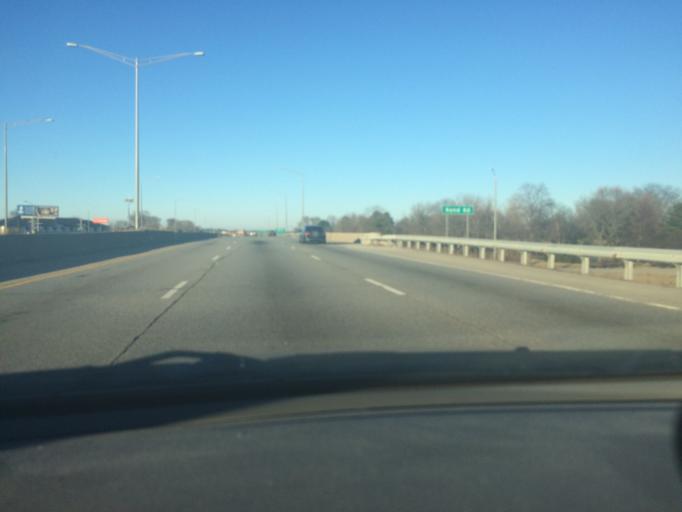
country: US
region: Illinois
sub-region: Cook County
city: Palatine
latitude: 42.1286
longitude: -88.0047
